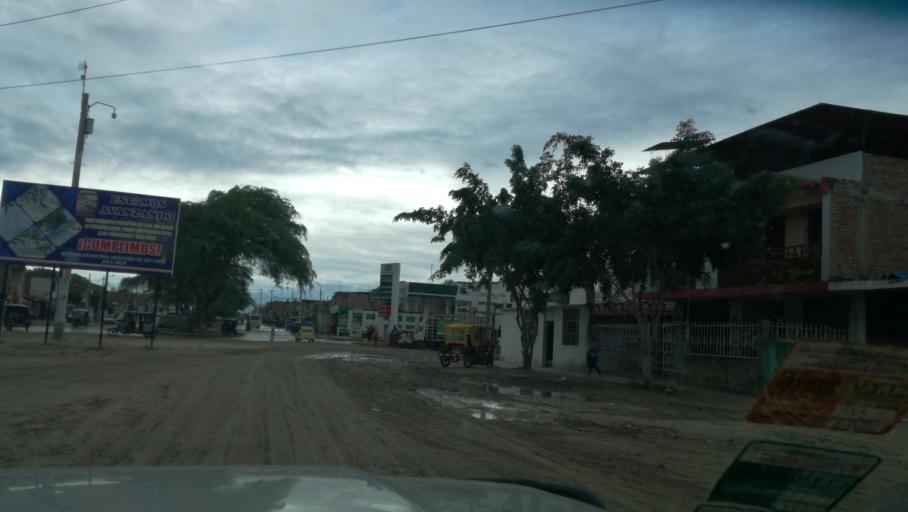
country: PE
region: Piura
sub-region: Provincia de Piura
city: Piura
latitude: -5.1889
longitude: -80.6667
